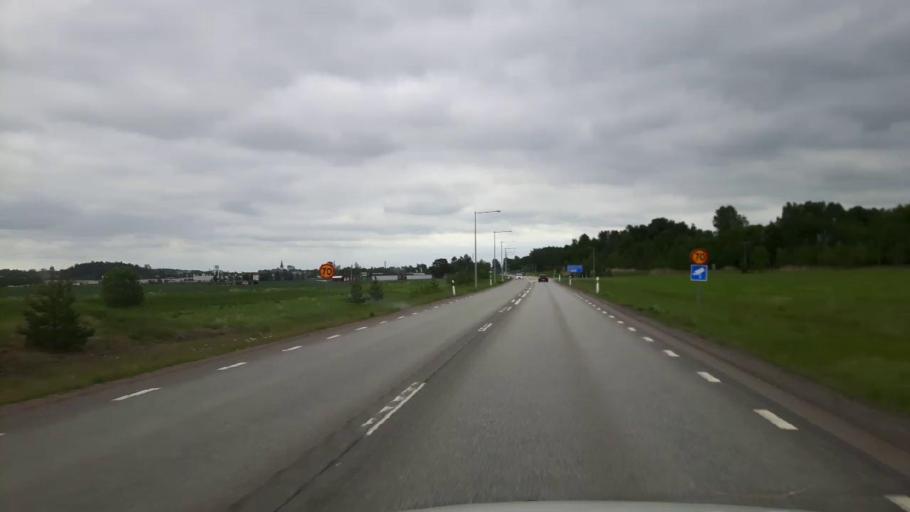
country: SE
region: Vaestmanland
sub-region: Kopings Kommun
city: Koping
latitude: 59.5296
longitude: 15.9588
